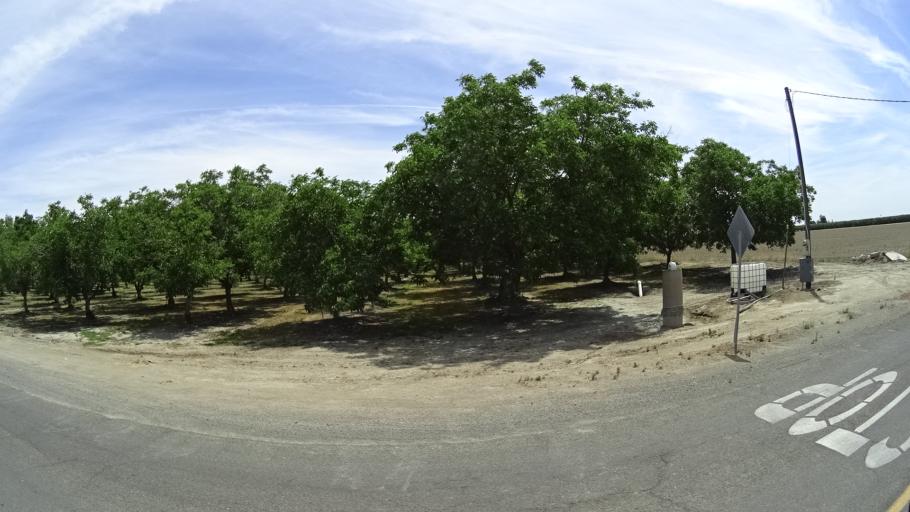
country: US
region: California
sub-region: Kings County
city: Lucerne
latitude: 36.3996
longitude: -119.6910
